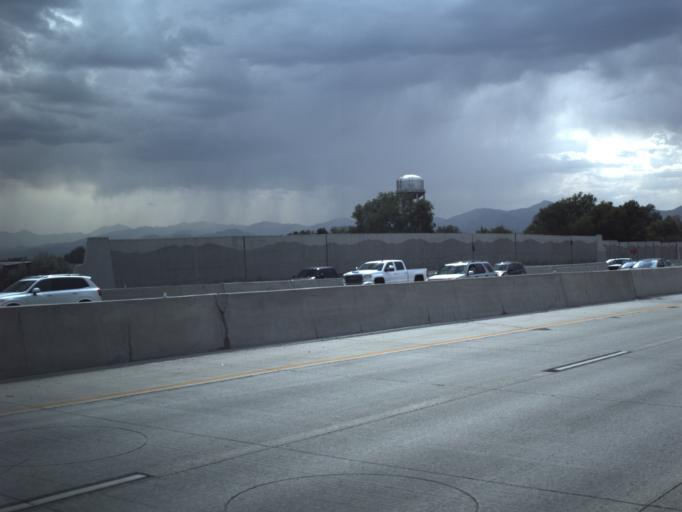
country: US
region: Utah
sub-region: Salt Lake County
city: South Salt Lake
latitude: 40.7184
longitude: -111.8903
